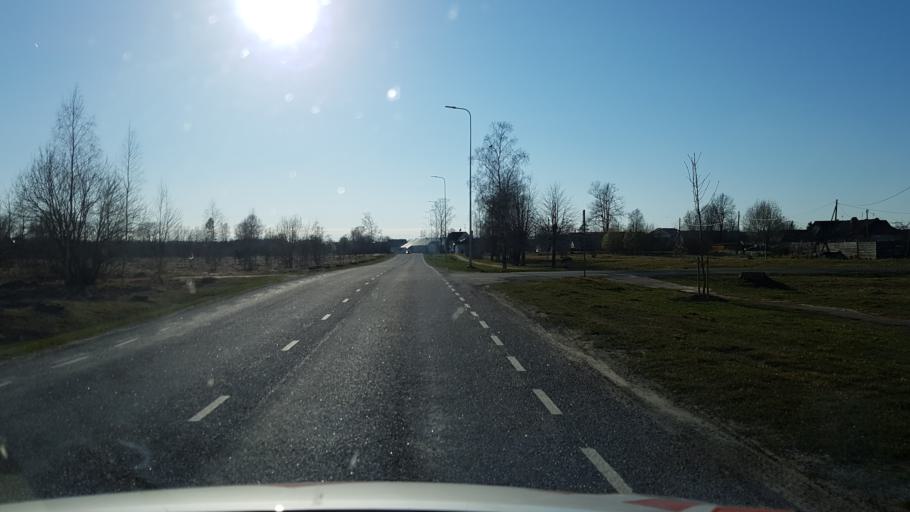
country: EE
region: Ida-Virumaa
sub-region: Kohtla-Jaerve linn
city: Kohtla-Jarve
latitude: 59.3372
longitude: 27.2980
